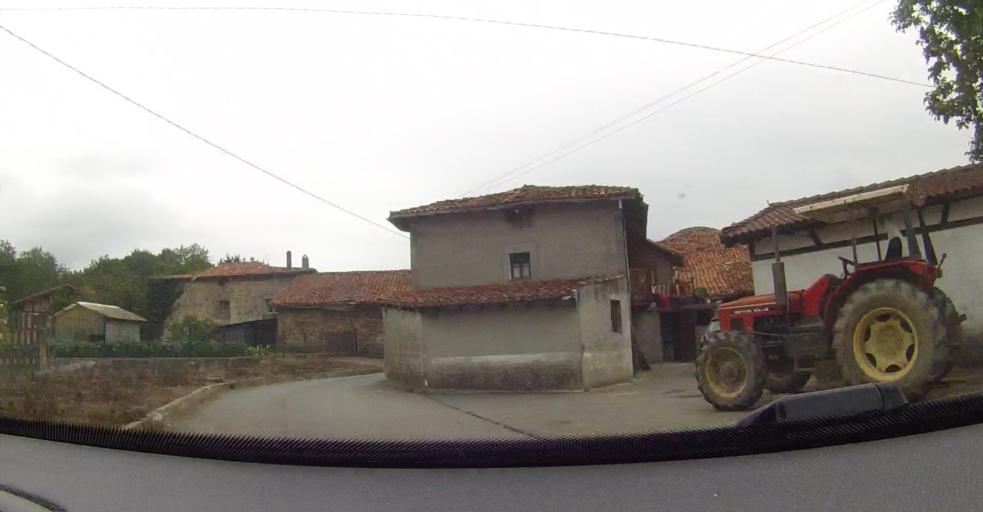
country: ES
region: Basque Country
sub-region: Bizkaia
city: Urrestieta
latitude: 43.2345
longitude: -3.1856
